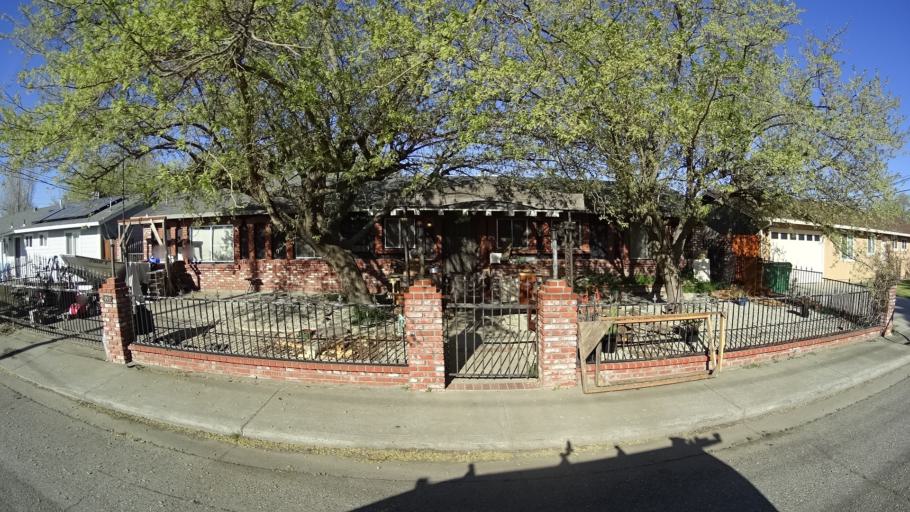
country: US
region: California
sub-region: Glenn County
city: Orland
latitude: 39.7579
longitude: -122.2202
